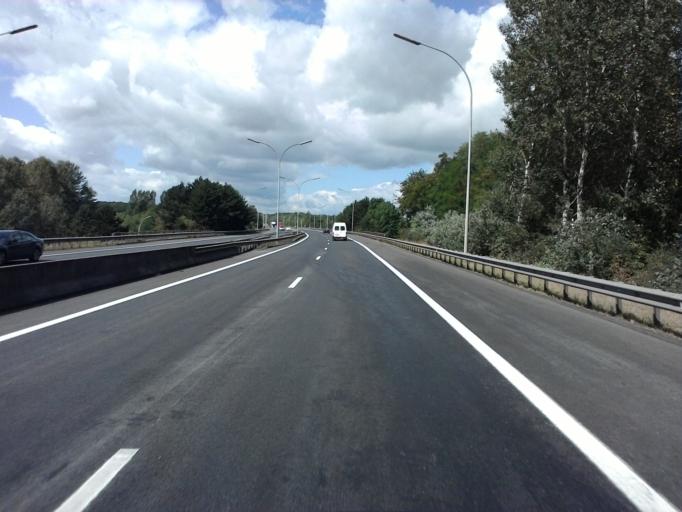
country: LU
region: Luxembourg
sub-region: Canton de Capellen
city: Mamer
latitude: 49.6389
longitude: 6.0092
